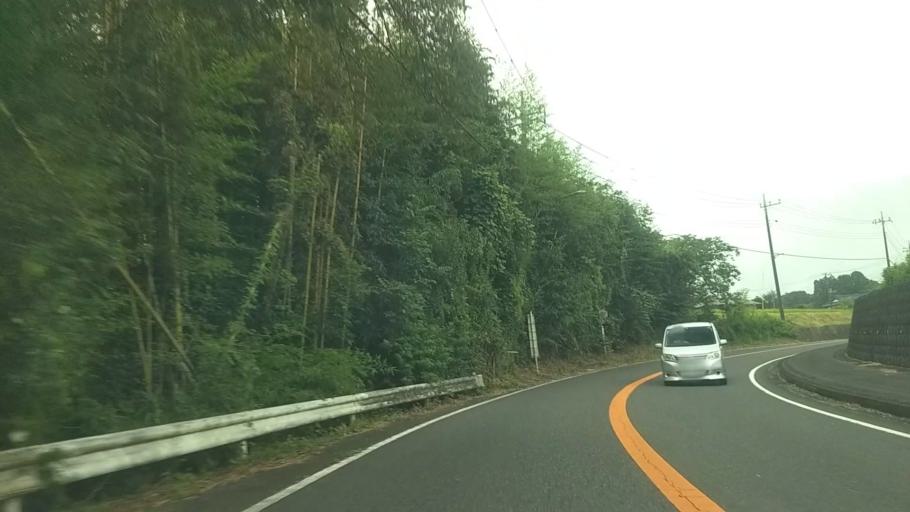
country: JP
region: Chiba
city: Kawaguchi
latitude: 35.2454
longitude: 140.0783
